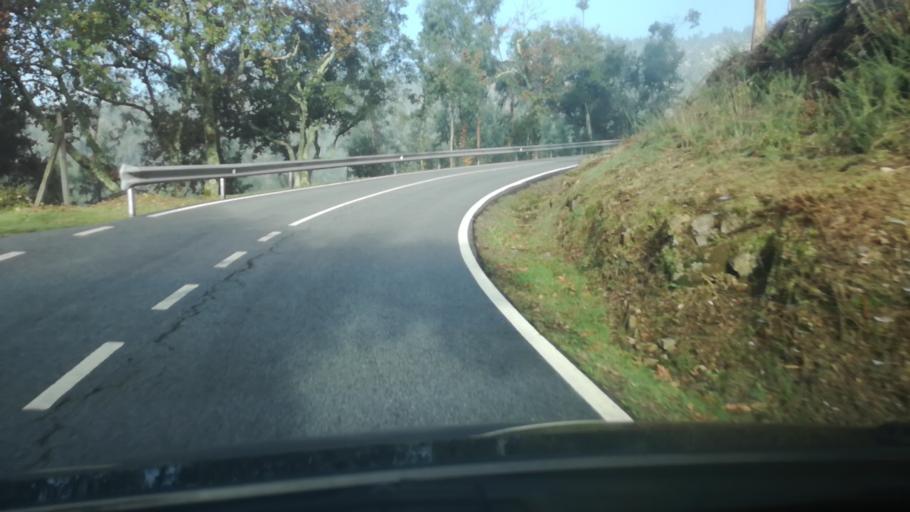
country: PT
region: Braga
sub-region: Guimaraes
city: Ponte
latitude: 41.5282
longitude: -8.3205
